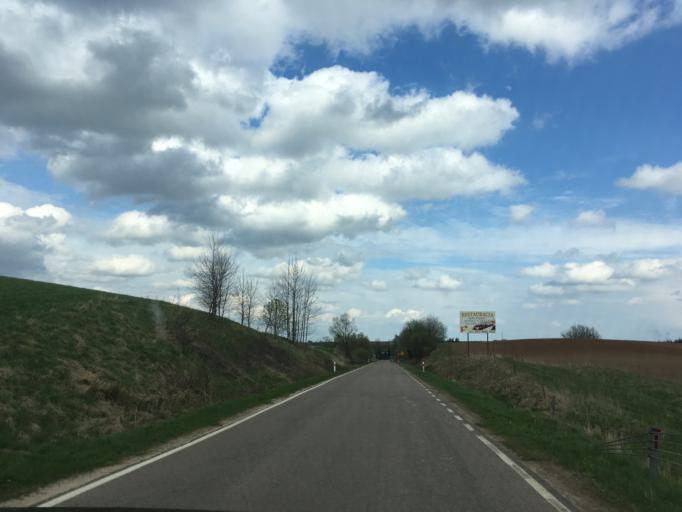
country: PL
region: Podlasie
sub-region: Suwalki
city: Suwalki
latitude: 54.3639
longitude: 22.8502
